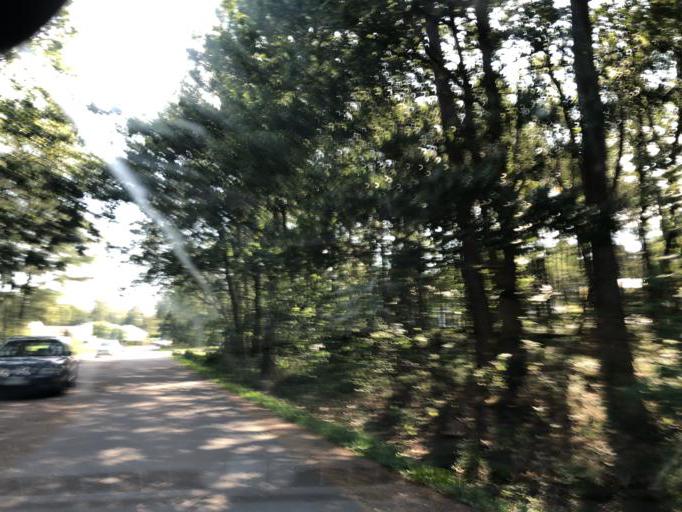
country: SE
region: Vaestra Goetaland
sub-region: Goteborg
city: Goeteborg
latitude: 57.7618
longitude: 11.9635
